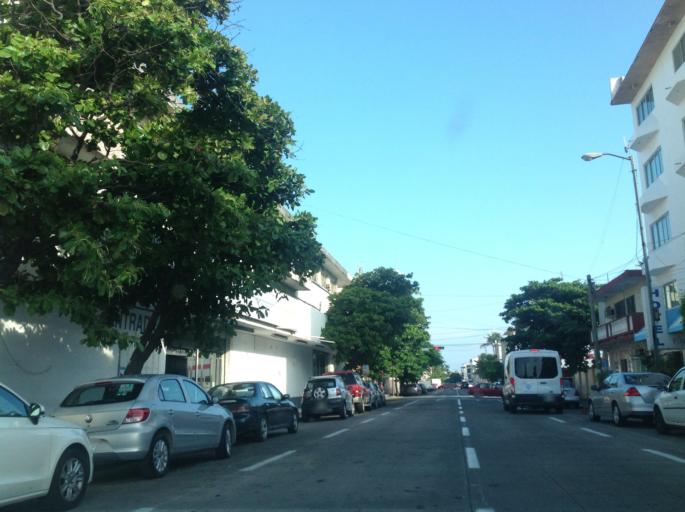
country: MX
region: Veracruz
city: Veracruz
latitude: 19.2001
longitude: -96.1341
